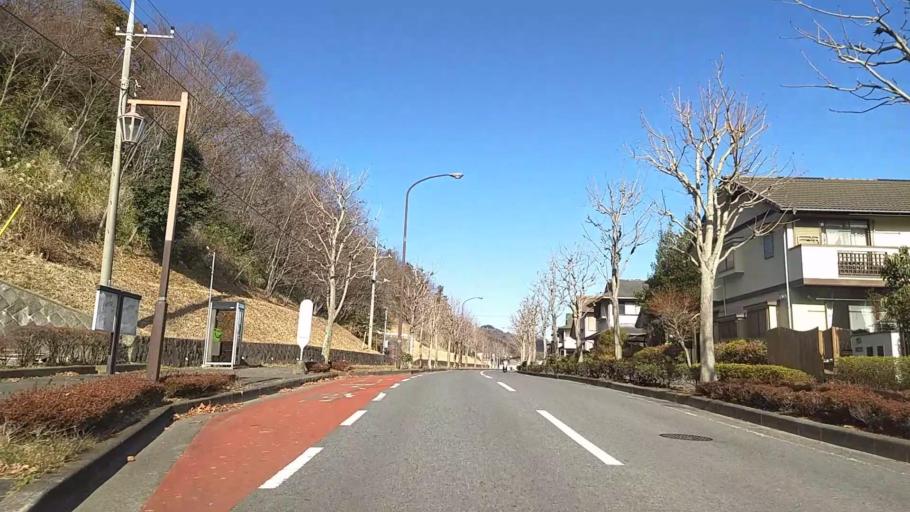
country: JP
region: Kanagawa
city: Atsugi
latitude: 35.4489
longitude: 139.3041
